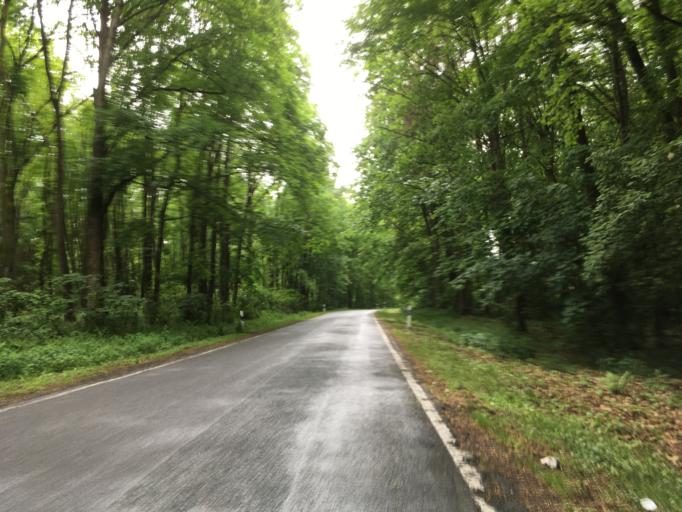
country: DE
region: Brandenburg
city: Werftpfuhl
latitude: 52.7336
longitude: 13.8130
